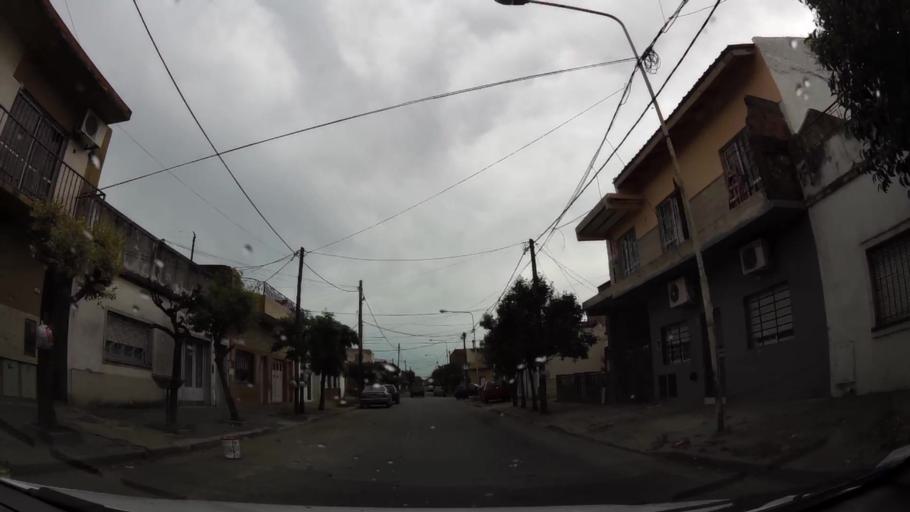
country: AR
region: Buenos Aires
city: San Justo
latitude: -34.6697
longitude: -58.5232
